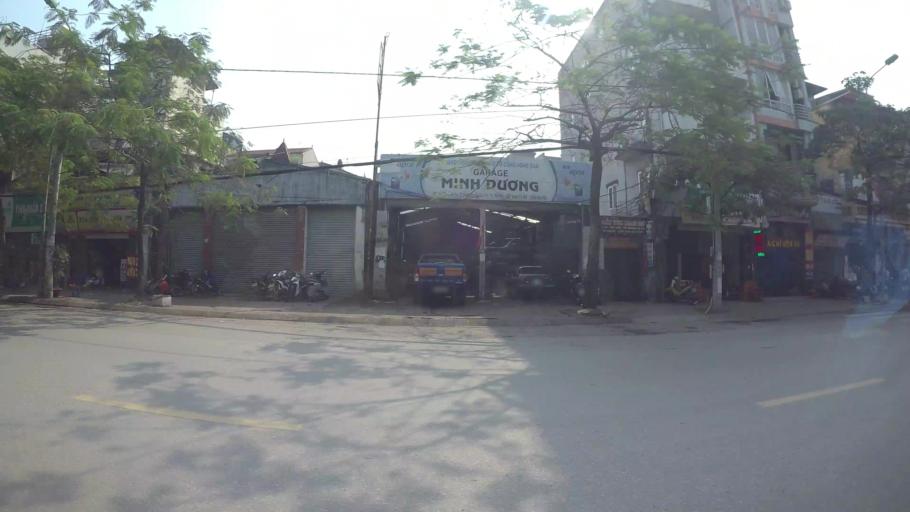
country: VN
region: Ha Noi
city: Tay Ho
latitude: 21.0627
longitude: 105.8077
